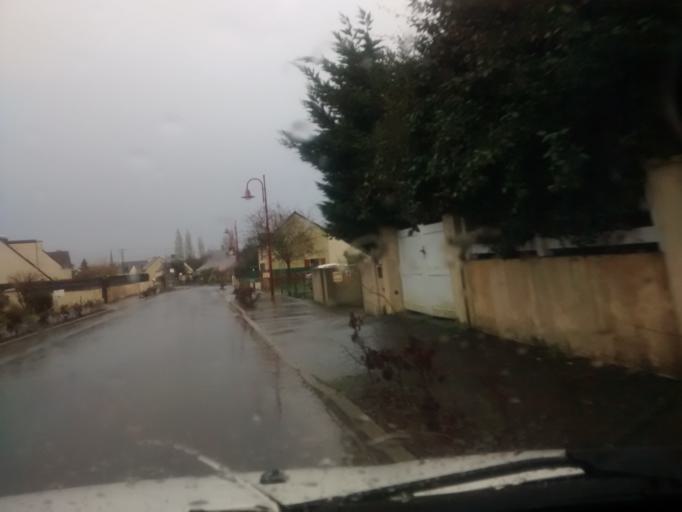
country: FR
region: Brittany
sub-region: Departement d'Ille-et-Vilaine
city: La Gouesniere
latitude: 48.5777
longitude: -1.8888
